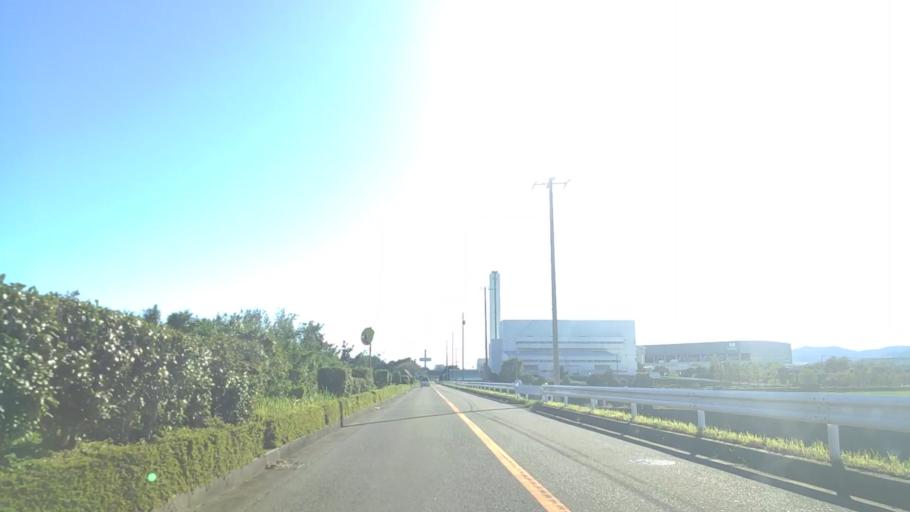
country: JP
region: Kanagawa
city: Atsugi
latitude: 35.4606
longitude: 139.3761
